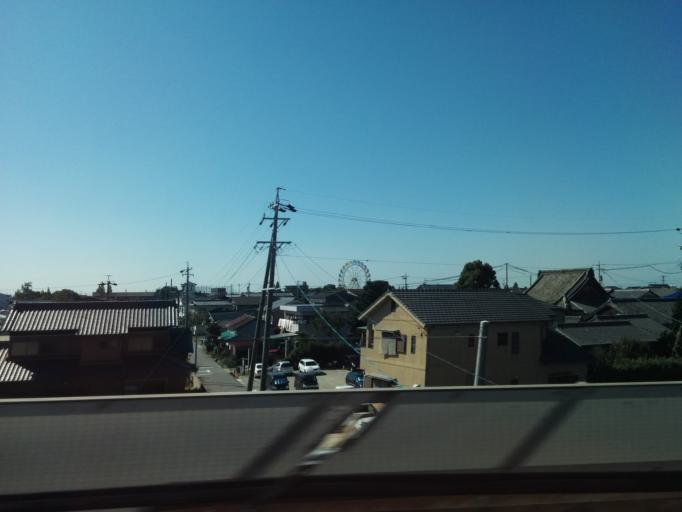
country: JP
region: Aichi
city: Anjo
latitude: 34.9314
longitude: 137.0951
